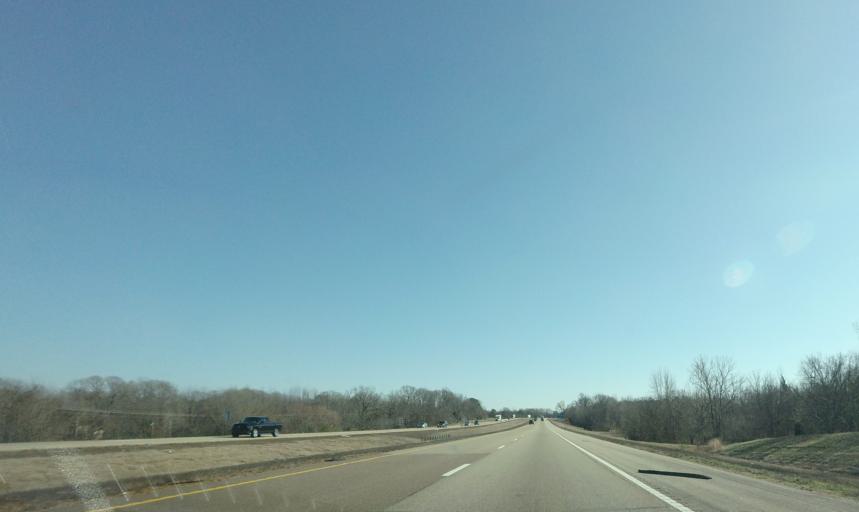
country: US
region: Mississippi
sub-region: Marshall County
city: Holly Springs
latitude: 34.8057
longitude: -89.5074
